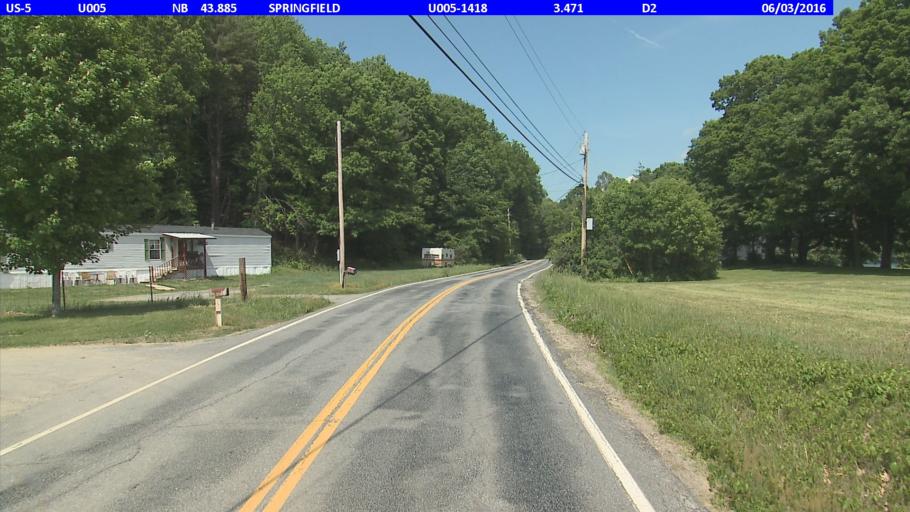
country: US
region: New Hampshire
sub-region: Sullivan County
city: Charlestown
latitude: 43.2657
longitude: -72.4225
